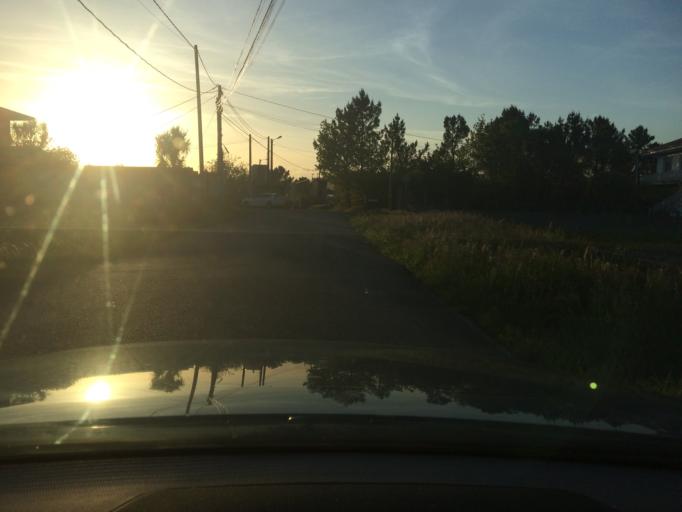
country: ES
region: Galicia
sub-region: Provincia da Coruna
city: Ames
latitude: 42.8339
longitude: -8.6021
